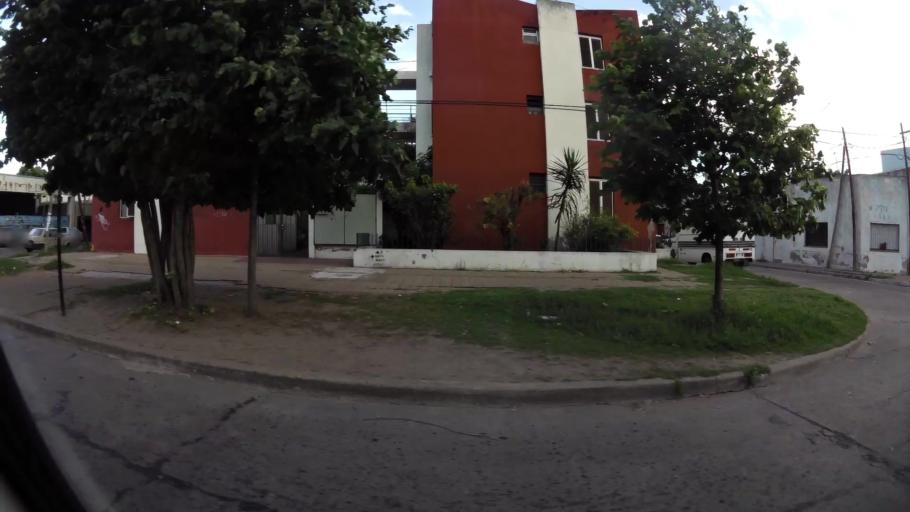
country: AR
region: Buenos Aires
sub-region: Partido de La Plata
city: La Plata
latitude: -34.8942
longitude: -57.9617
